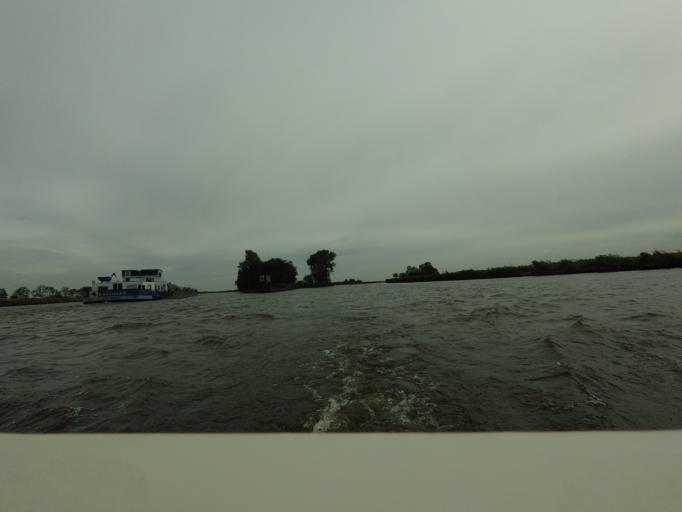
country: NL
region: Friesland
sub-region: Gemeente Boarnsterhim
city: Grou
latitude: 53.1104
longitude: 5.8659
